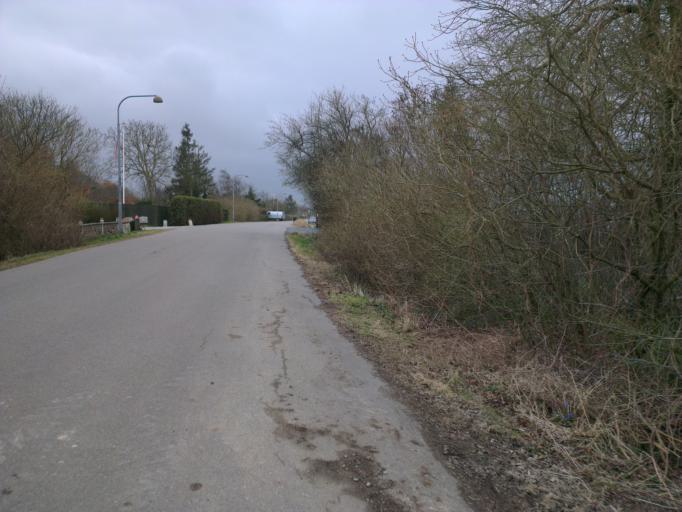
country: DK
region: Capital Region
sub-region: Frederikssund Kommune
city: Frederikssund
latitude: 55.8788
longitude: 12.0707
